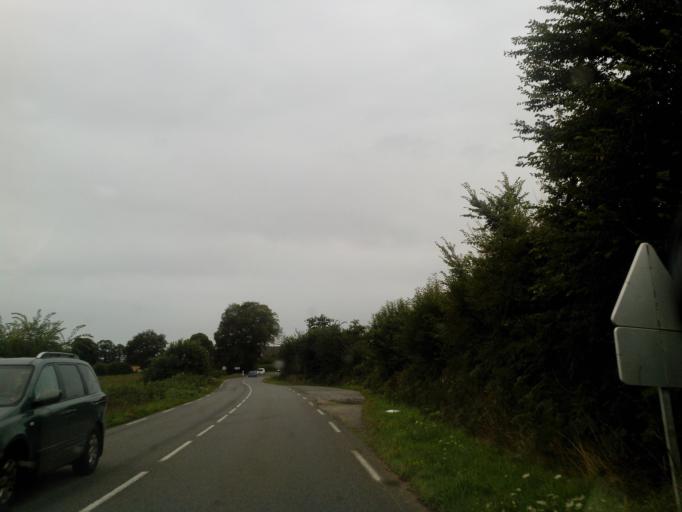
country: FR
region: Brittany
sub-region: Departement du Finistere
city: Tremeven
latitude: 47.8869
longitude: -3.5313
